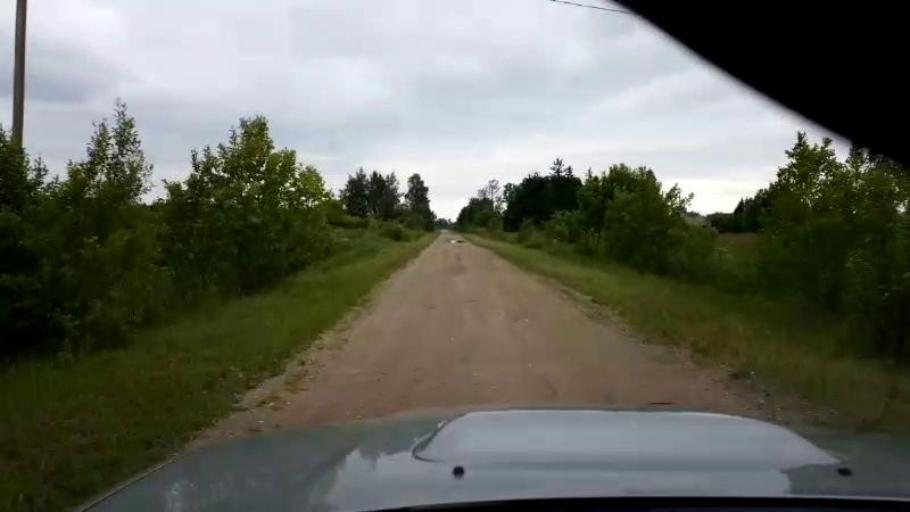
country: EE
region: Paernumaa
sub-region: Halinga vald
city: Parnu-Jaagupi
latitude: 58.5582
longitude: 24.5756
